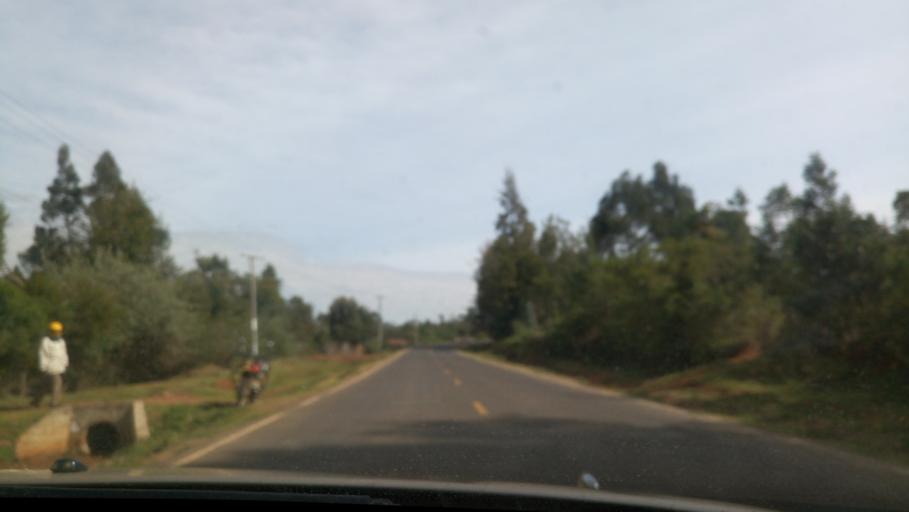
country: KE
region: Laikipia
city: Nyahururu
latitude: 0.0110
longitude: 36.4121
